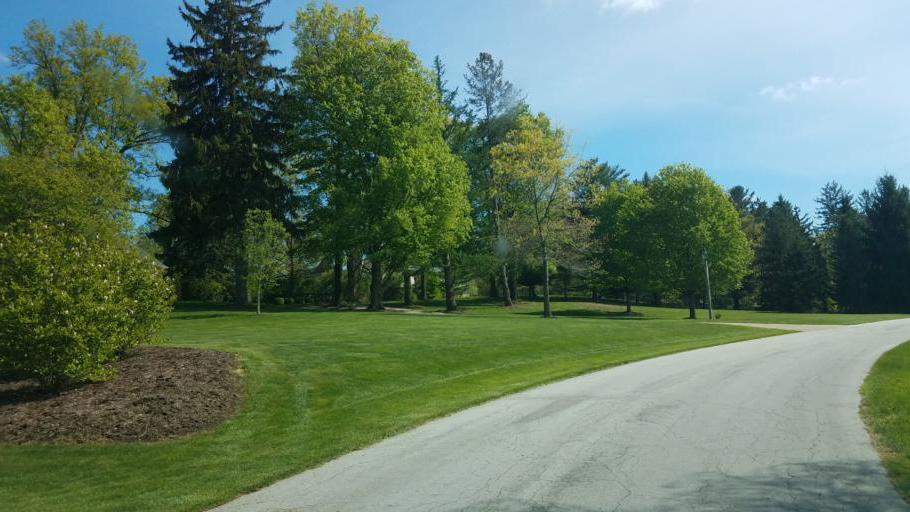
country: US
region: Ohio
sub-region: Richland County
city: Ontario
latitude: 40.7453
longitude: -82.5593
